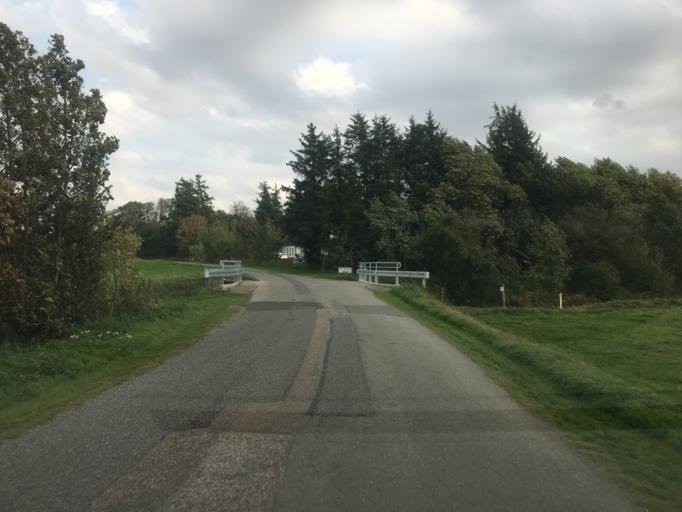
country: DK
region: South Denmark
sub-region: Tonder Kommune
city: Logumkloster
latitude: 55.0058
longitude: 9.0334
